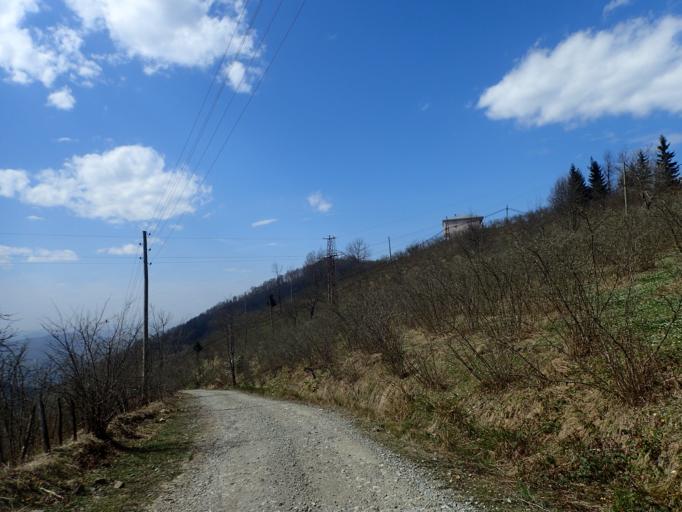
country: TR
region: Ordu
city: Kabaduz
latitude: 40.8166
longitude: 37.9071
